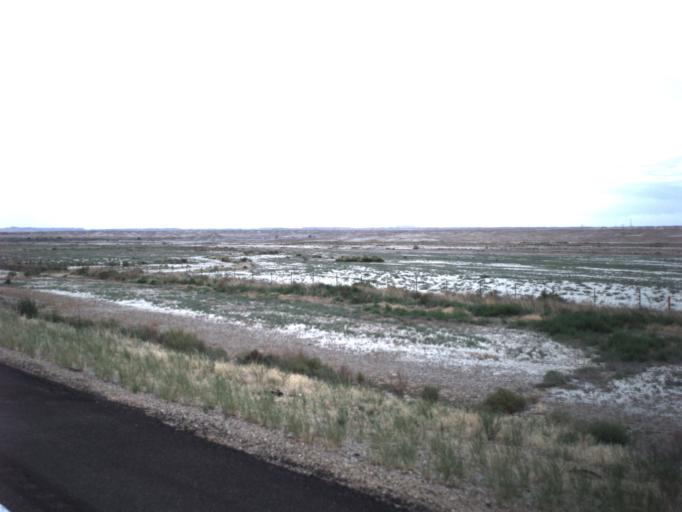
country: US
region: Utah
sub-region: Carbon County
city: East Carbon City
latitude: 39.0077
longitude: -110.2788
